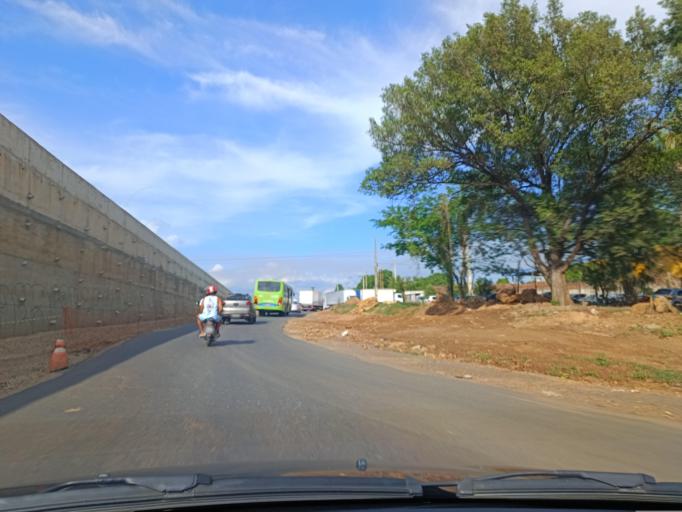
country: BR
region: Piaui
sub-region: Teresina
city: Teresina
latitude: -5.0897
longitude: -42.7598
